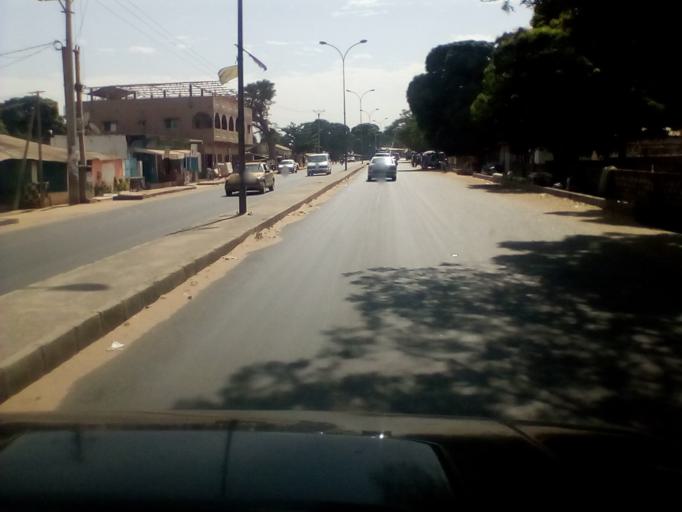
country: GM
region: Western
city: Abuko
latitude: 13.3841
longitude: -16.6436
